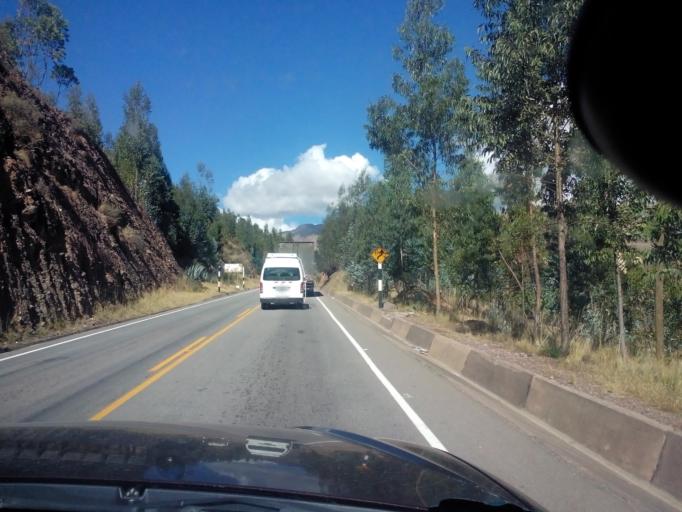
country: PE
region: Cusco
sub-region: Provincia de Quispicanchis
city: Urcos
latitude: -13.6888
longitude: -71.5943
